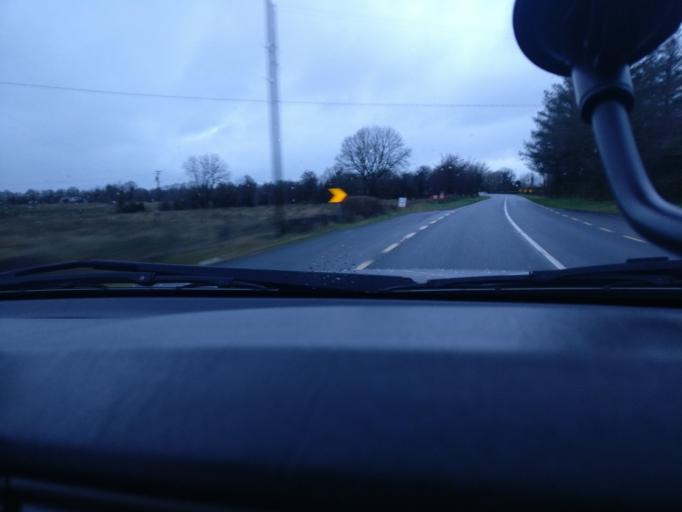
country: IE
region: Connaught
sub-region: County Galway
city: Ballinasloe
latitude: 53.2841
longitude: -8.3555
